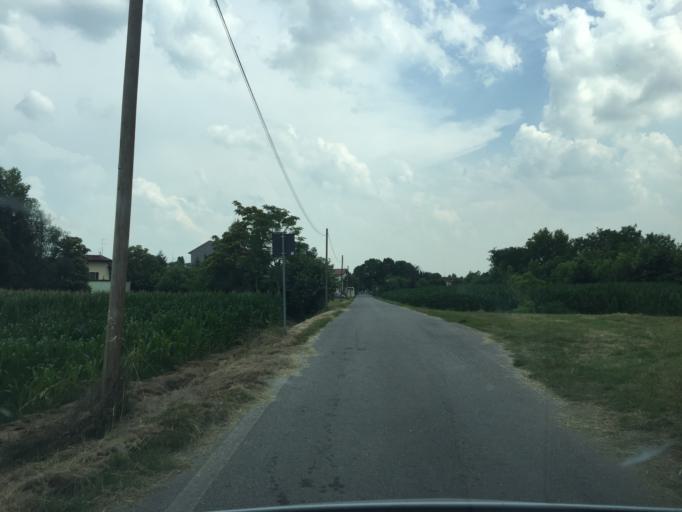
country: IT
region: Lombardy
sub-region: Provincia di Brescia
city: Flero
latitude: 45.4908
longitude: 10.1748
